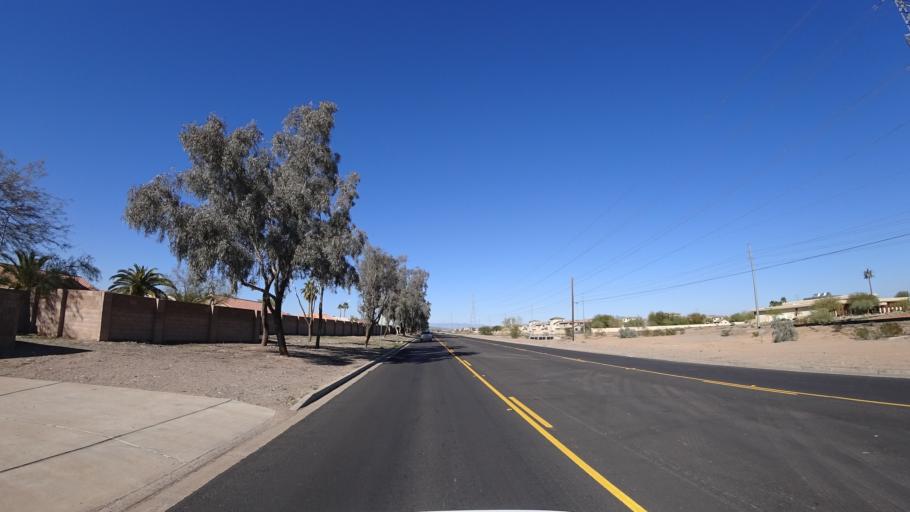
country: US
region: Arizona
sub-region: Maricopa County
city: Surprise
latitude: 33.6414
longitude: -112.3078
